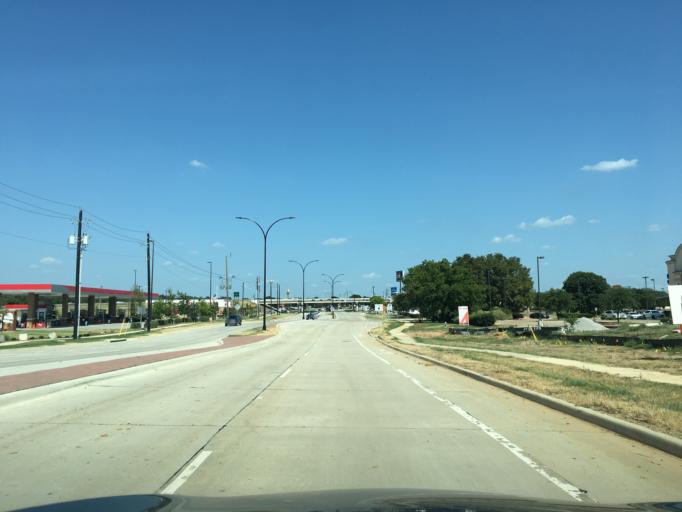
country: US
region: Texas
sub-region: Tarrant County
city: Kennedale
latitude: 32.6462
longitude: -97.1889
